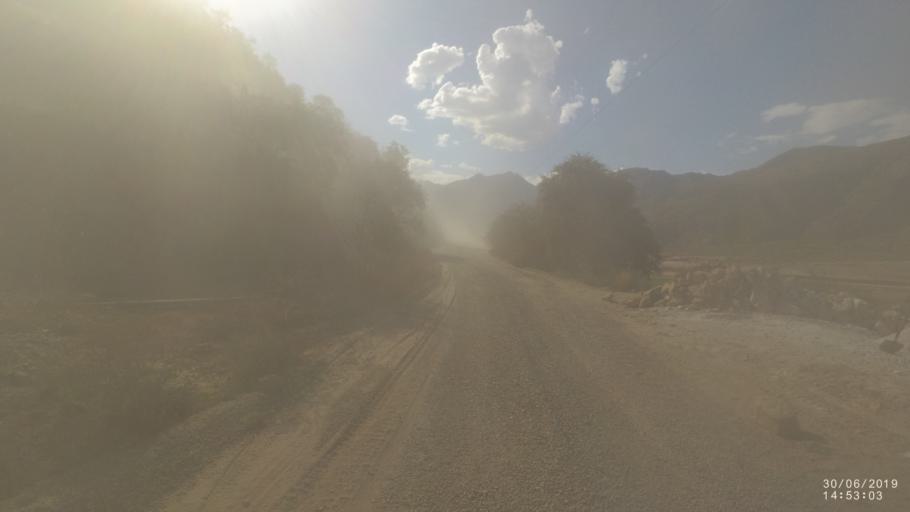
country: BO
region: Cochabamba
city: Irpa Irpa
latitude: -17.7661
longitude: -66.3479
